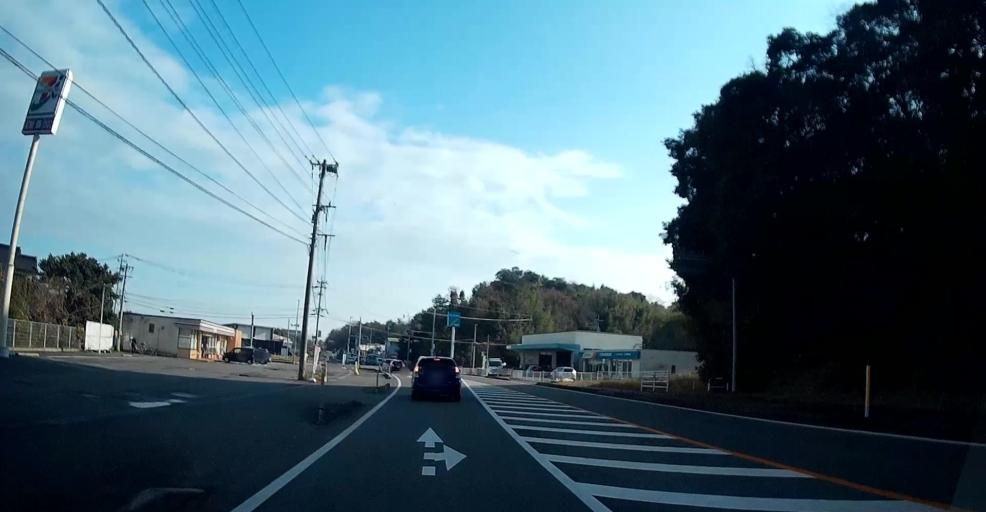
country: JP
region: Kumamoto
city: Yatsushiro
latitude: 32.5532
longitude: 130.4174
